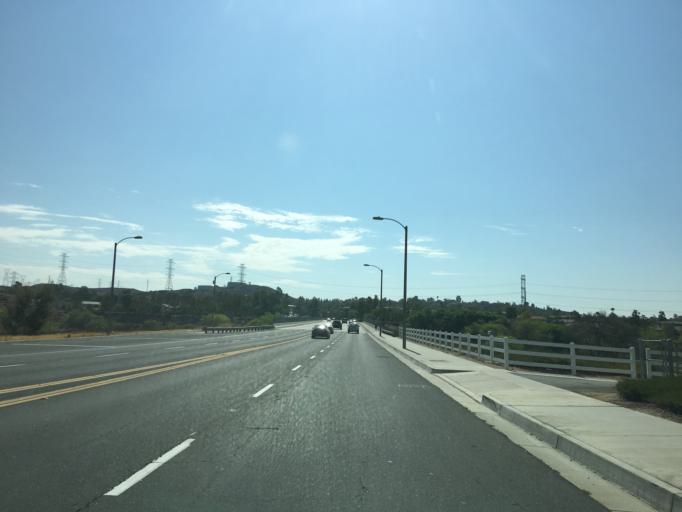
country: US
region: California
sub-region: Los Angeles County
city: Valencia
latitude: 34.4628
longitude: -118.5540
